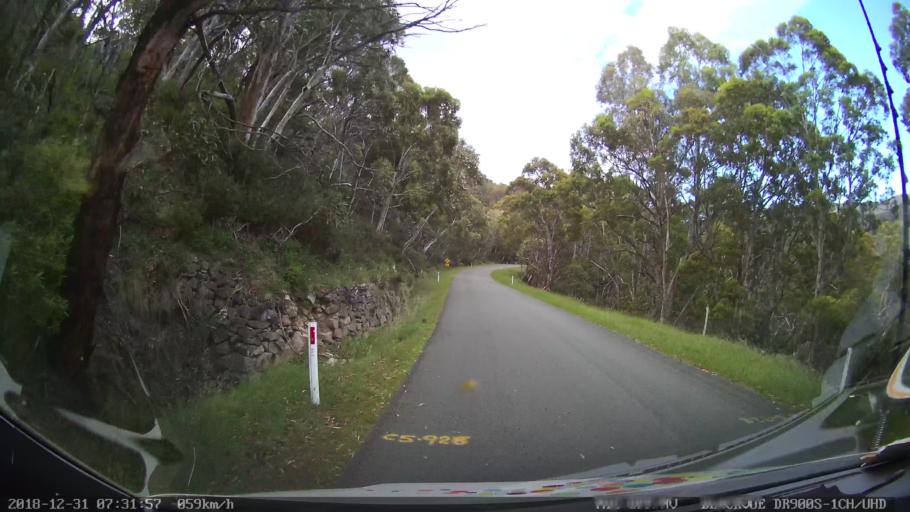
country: AU
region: New South Wales
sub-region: Snowy River
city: Jindabyne
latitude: -36.3287
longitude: 148.4691
